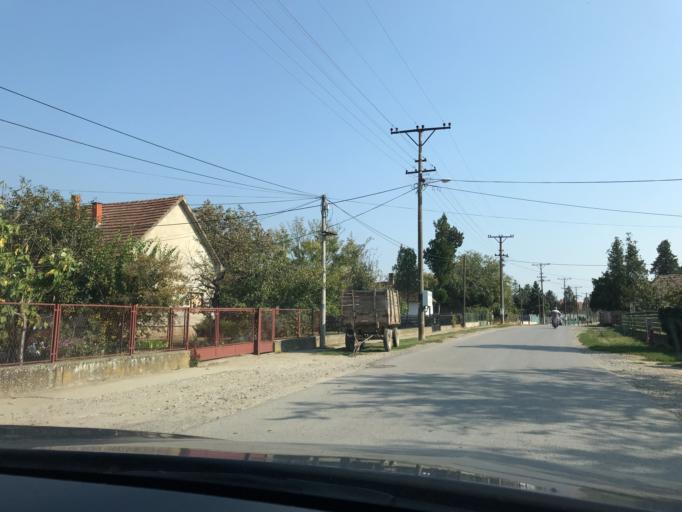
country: RS
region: Central Serbia
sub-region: Belgrade
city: Obrenovac
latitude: 44.6825
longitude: 20.2122
